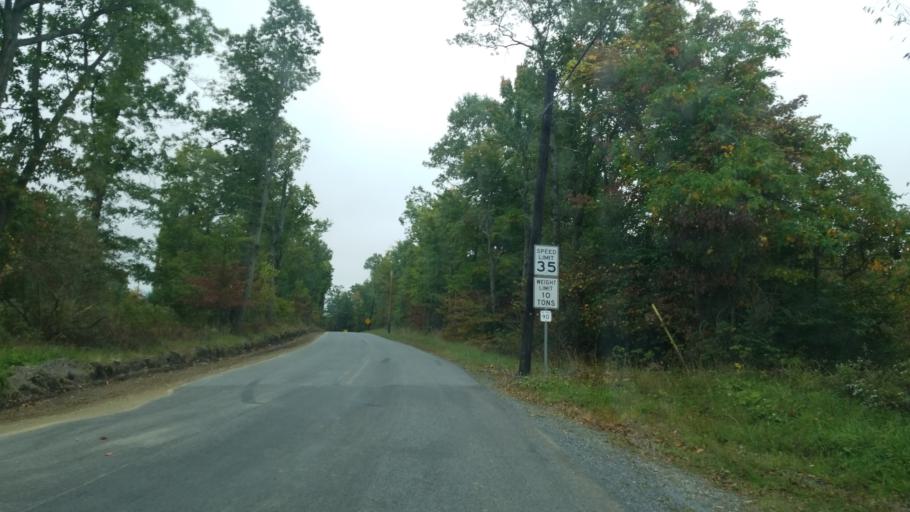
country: US
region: Pennsylvania
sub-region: Clearfield County
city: Curwensville
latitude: 41.0305
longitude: -78.5580
